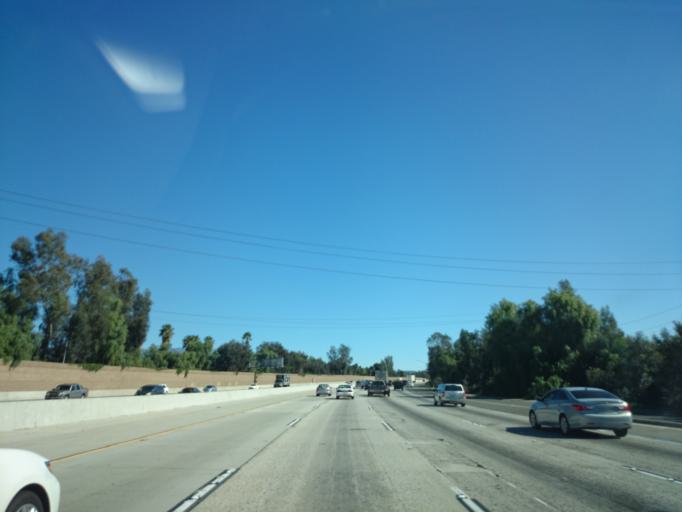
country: US
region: California
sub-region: San Bernardino County
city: Redlands
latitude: 34.0614
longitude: -117.1778
